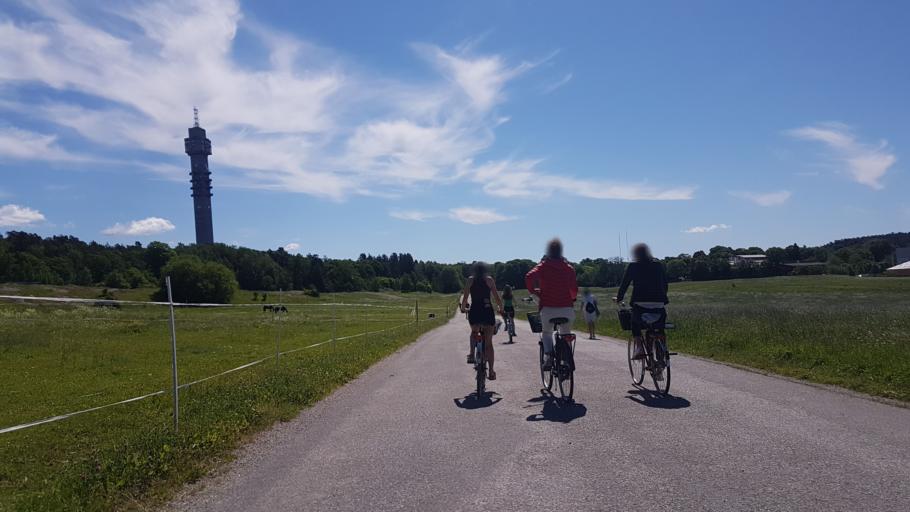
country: SE
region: Stockholm
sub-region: Stockholms Kommun
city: OEstermalm
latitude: 59.3371
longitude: 18.1163
